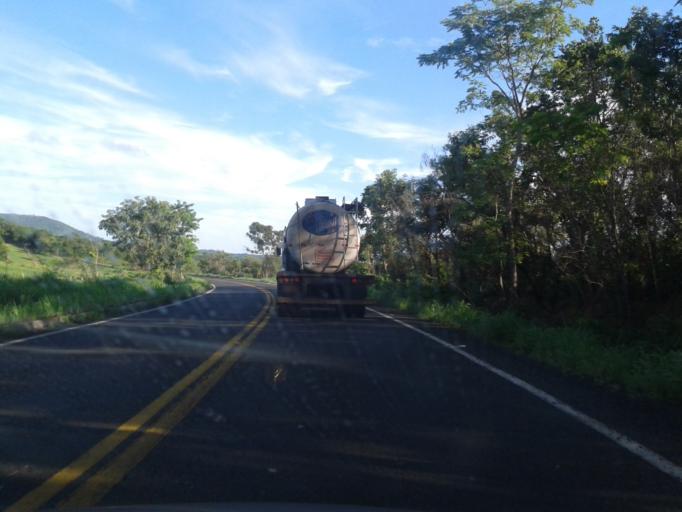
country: BR
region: Minas Gerais
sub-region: Tupaciguara
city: Tupaciguara
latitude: -18.2226
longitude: -48.5725
